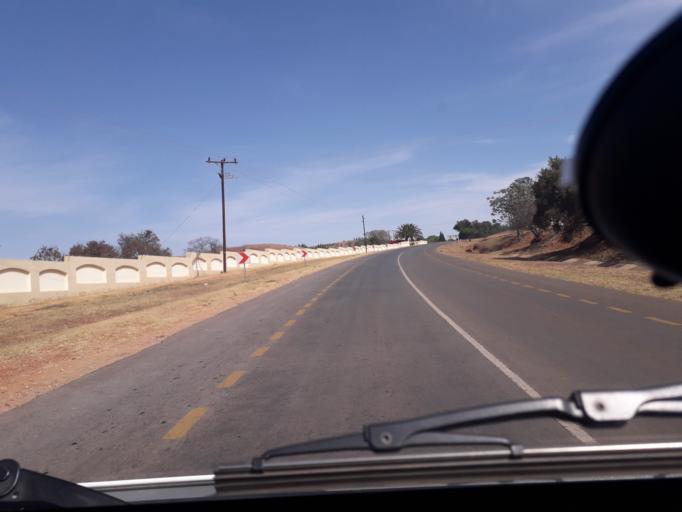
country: ZA
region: Gauteng
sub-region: West Rand District Municipality
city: Muldersdriseloop
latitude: -25.9901
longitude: 27.8259
